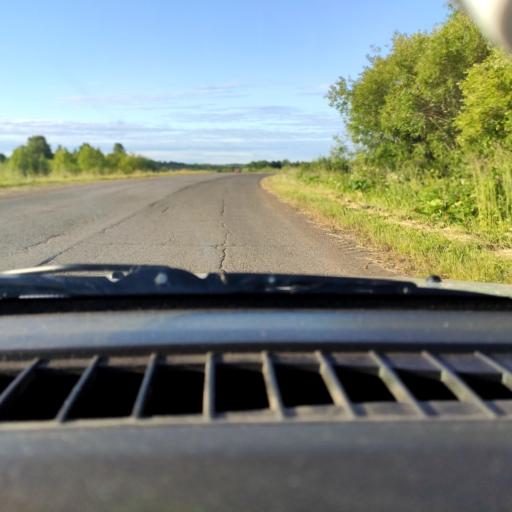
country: RU
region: Perm
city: Uinskoye
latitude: 57.0877
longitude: 56.5584
